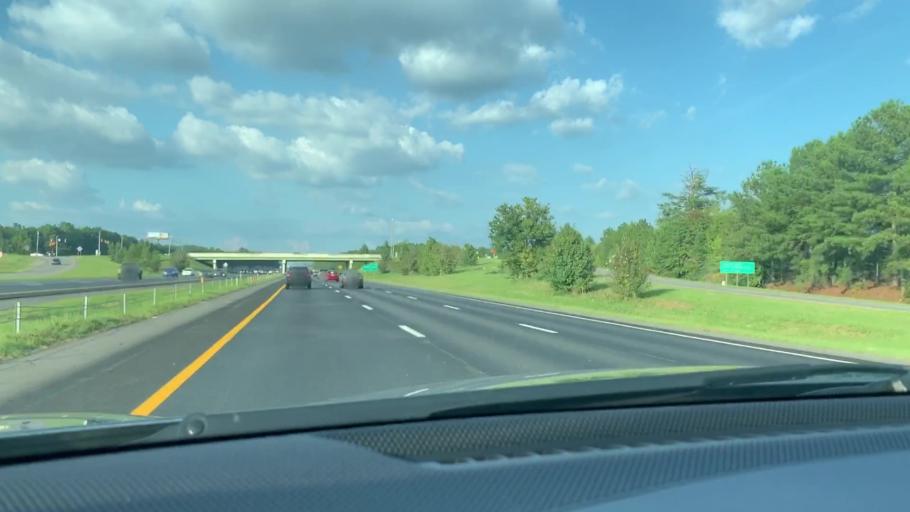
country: US
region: South Carolina
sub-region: Richland County
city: Forest Acres
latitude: 34.0190
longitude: -80.9477
